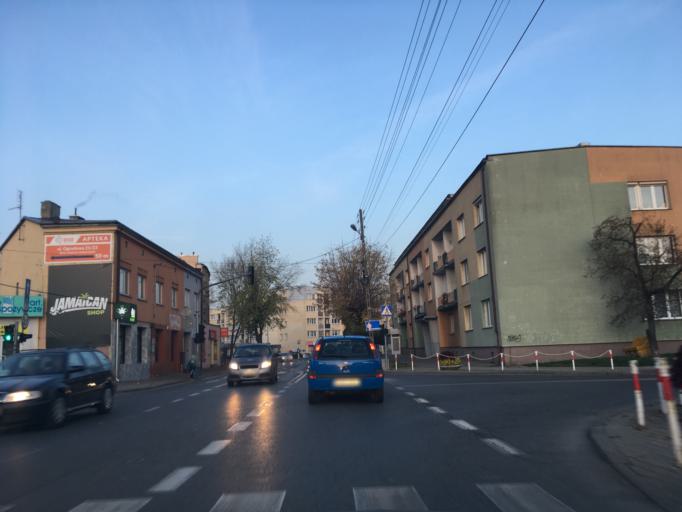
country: PL
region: Lodz Voivodeship
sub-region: Skierniewice
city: Skierniewice
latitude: 51.9564
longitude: 20.1468
